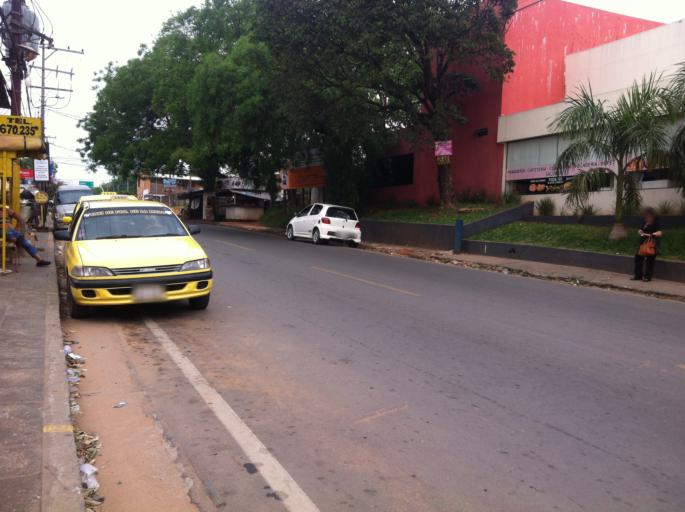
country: PY
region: Central
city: Fernando de la Mora
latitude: -25.3100
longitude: -57.5313
